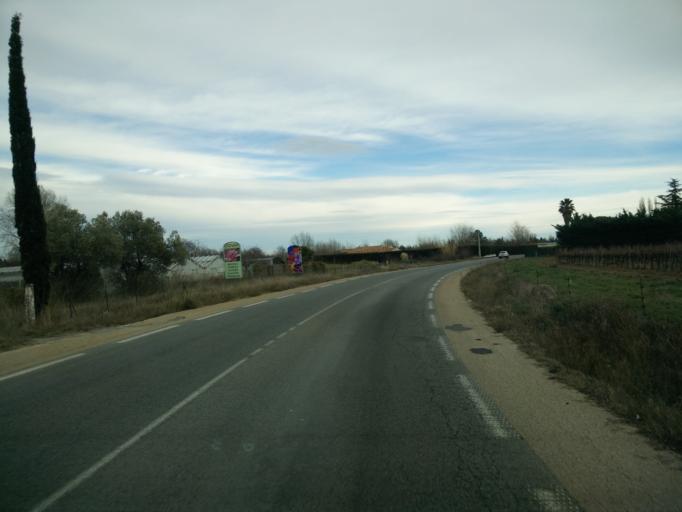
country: FR
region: Provence-Alpes-Cote d'Azur
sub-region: Departement du Var
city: Roquebrune-sur-Argens
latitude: 43.4419
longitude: 6.6523
